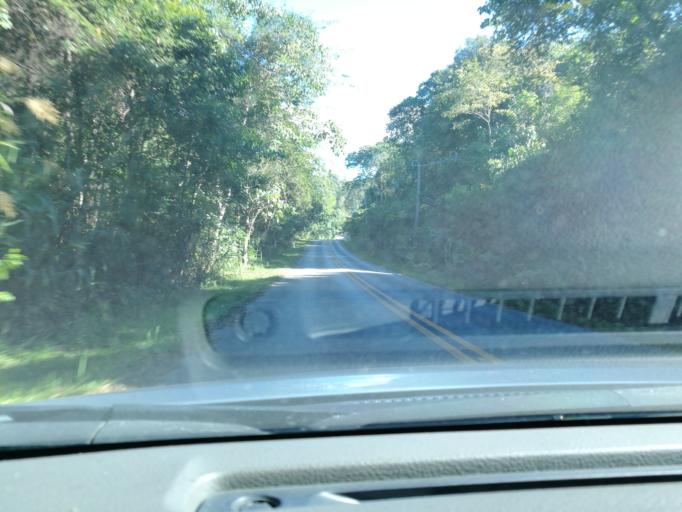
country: TH
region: Phitsanulok
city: Nakhon Thai
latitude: 16.9999
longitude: 100.9958
